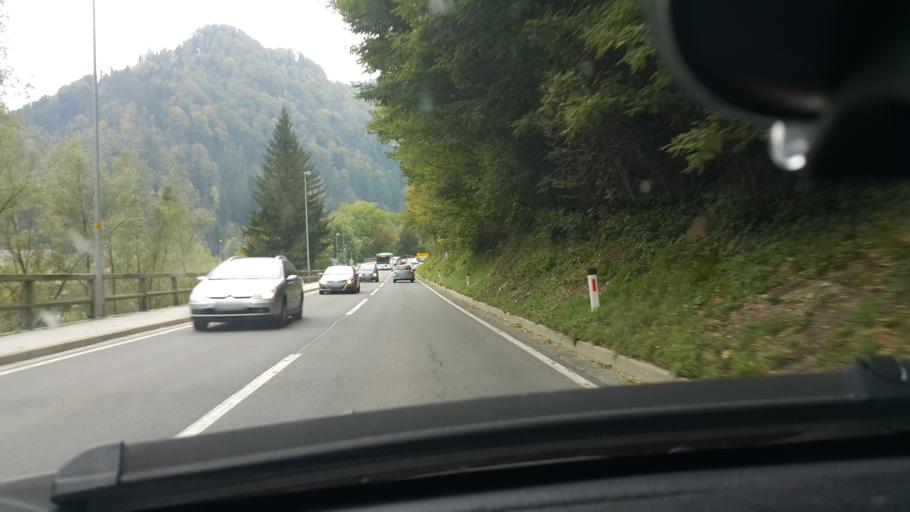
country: SI
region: Podvelka
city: Podvelka
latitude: 46.5917
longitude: 15.3287
